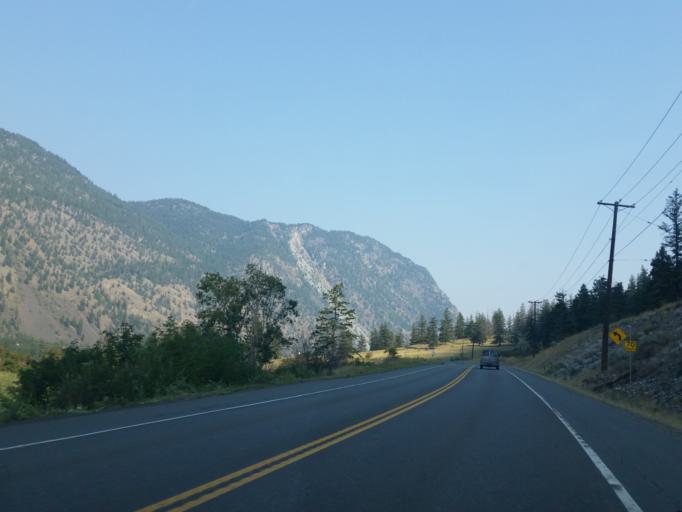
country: CA
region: British Columbia
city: Oliver
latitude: 49.2746
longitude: -120.0217
